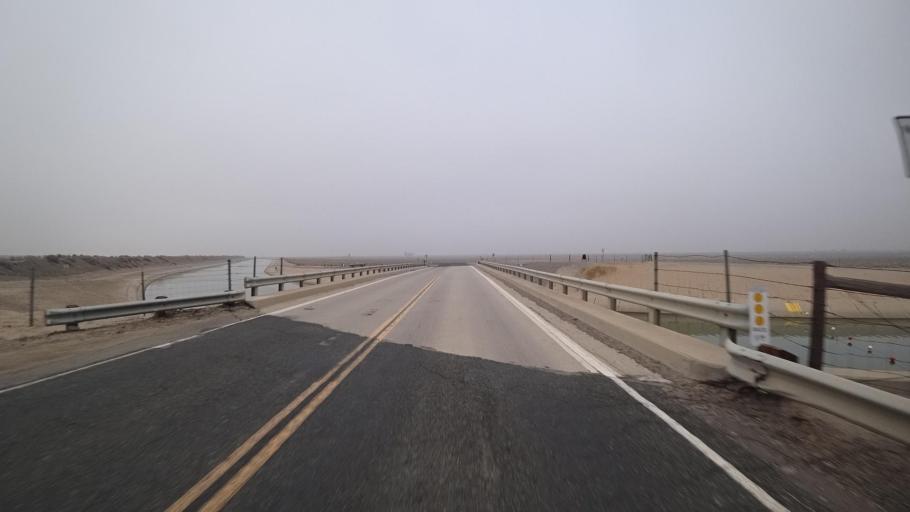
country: US
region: California
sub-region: Kern County
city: Buttonwillow
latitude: 35.3469
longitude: -119.4692
